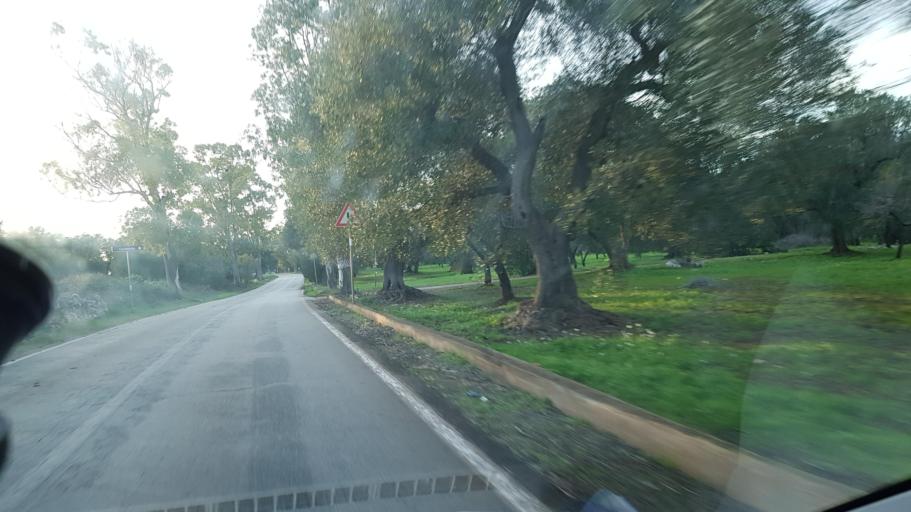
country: IT
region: Apulia
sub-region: Provincia di Brindisi
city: San Michele Salentino
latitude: 40.6426
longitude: 17.5965
